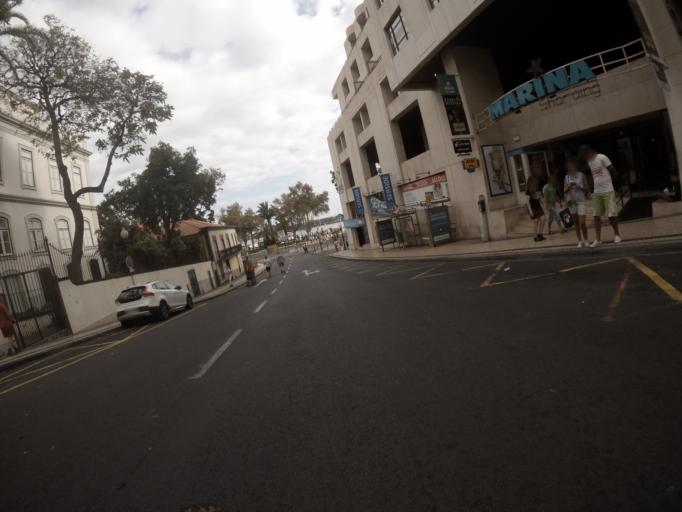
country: PT
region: Madeira
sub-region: Funchal
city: Funchal
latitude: 32.6469
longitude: -16.9118
